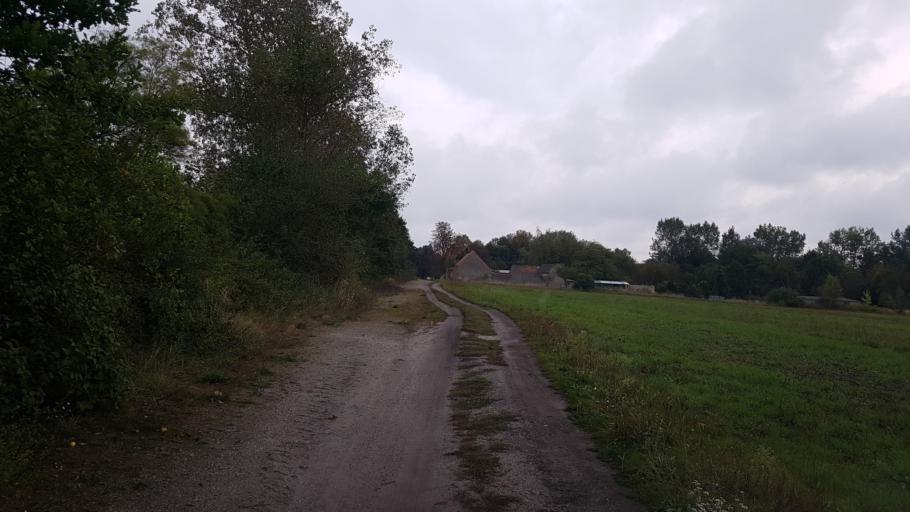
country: DE
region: Brandenburg
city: Lauchhammer
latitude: 51.4981
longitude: 13.7421
